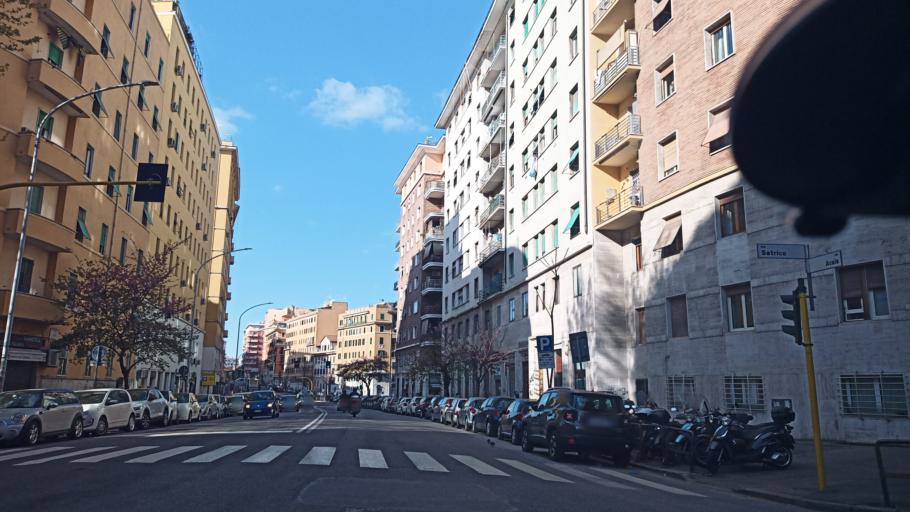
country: IT
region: Latium
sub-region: Citta metropolitana di Roma Capitale
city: Rome
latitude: 41.8768
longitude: 12.5082
